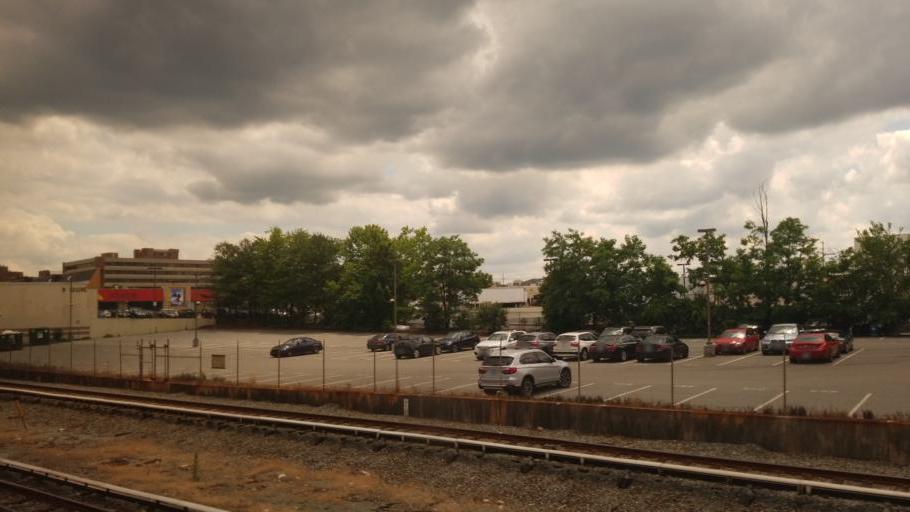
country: US
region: Maryland
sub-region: Montgomery County
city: North Bethesda
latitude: 39.0649
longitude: -77.1234
